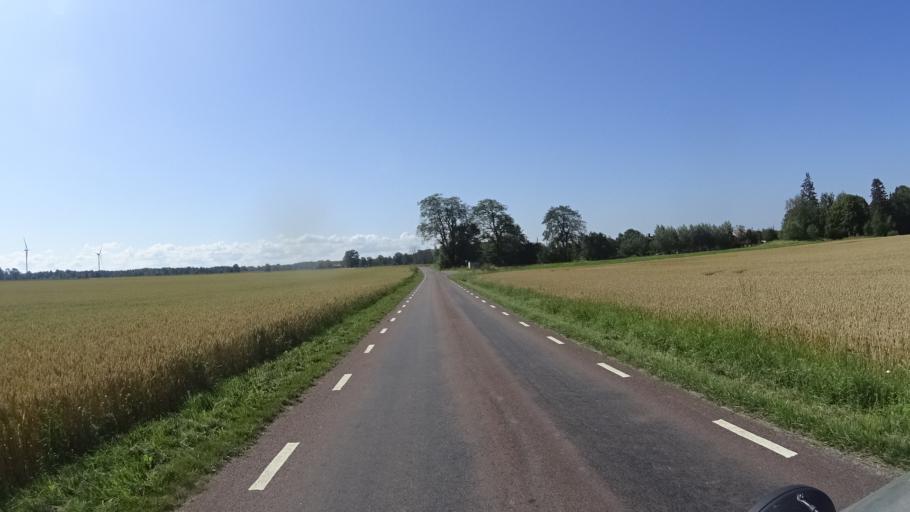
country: SE
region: OEstergoetland
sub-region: Vadstena Kommun
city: Herrestad
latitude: 58.3110
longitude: 14.8438
